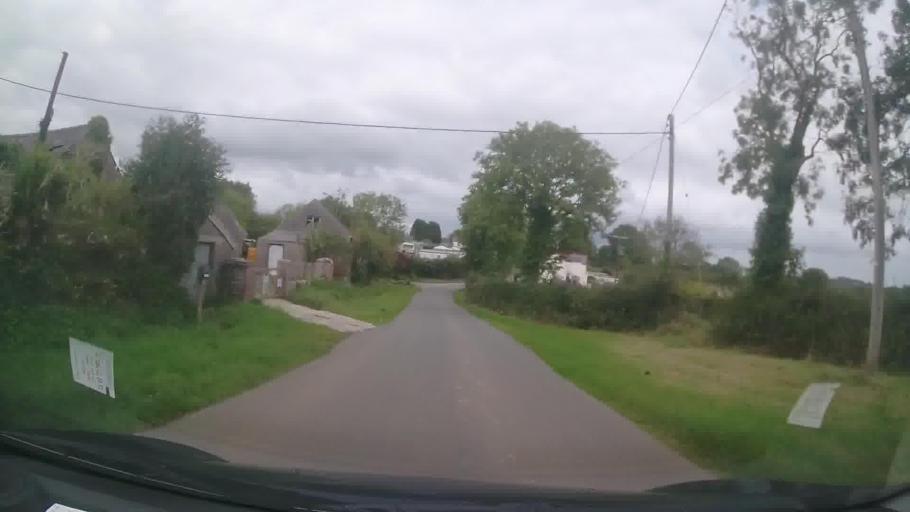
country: GB
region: Wales
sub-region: Pembrokeshire
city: Saundersfoot
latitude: 51.7505
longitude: -4.6545
